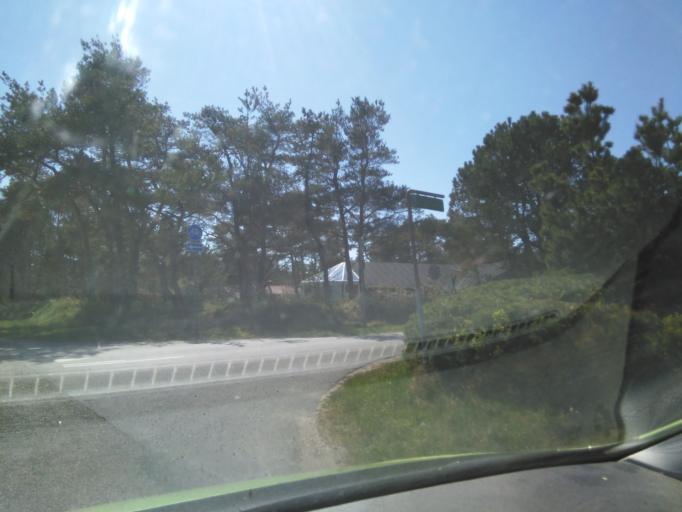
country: DK
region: South Denmark
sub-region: Varde Kommune
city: Oksbol
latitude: 55.5595
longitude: 8.2265
